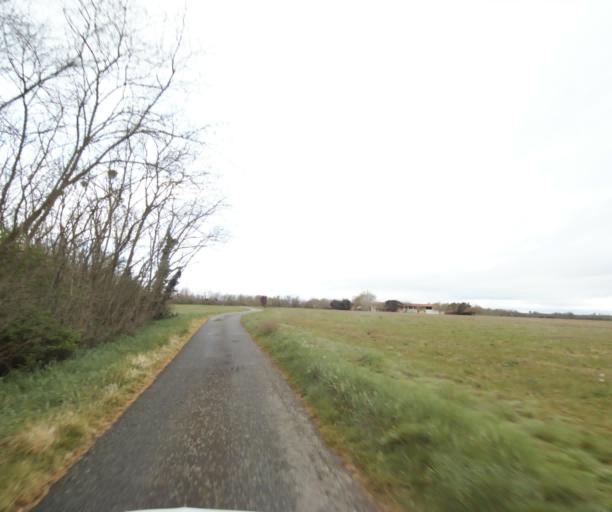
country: FR
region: Midi-Pyrenees
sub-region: Departement de l'Ariege
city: Saverdun
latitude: 43.2138
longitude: 1.6009
